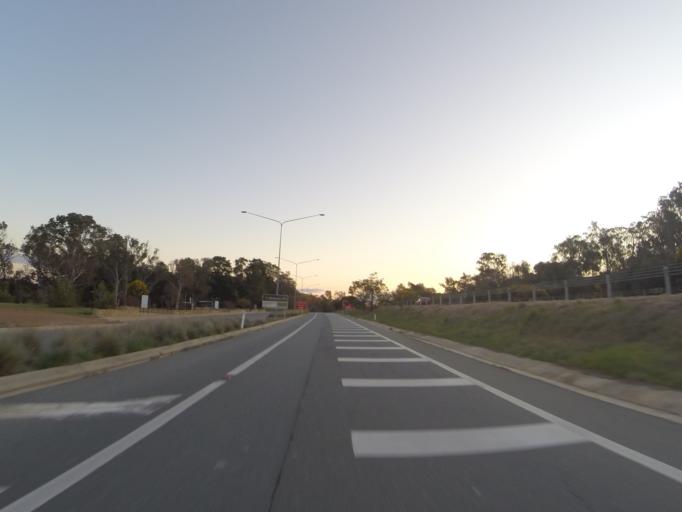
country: AU
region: Australian Capital Territory
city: Kaleen
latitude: -35.2106
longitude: 149.1907
